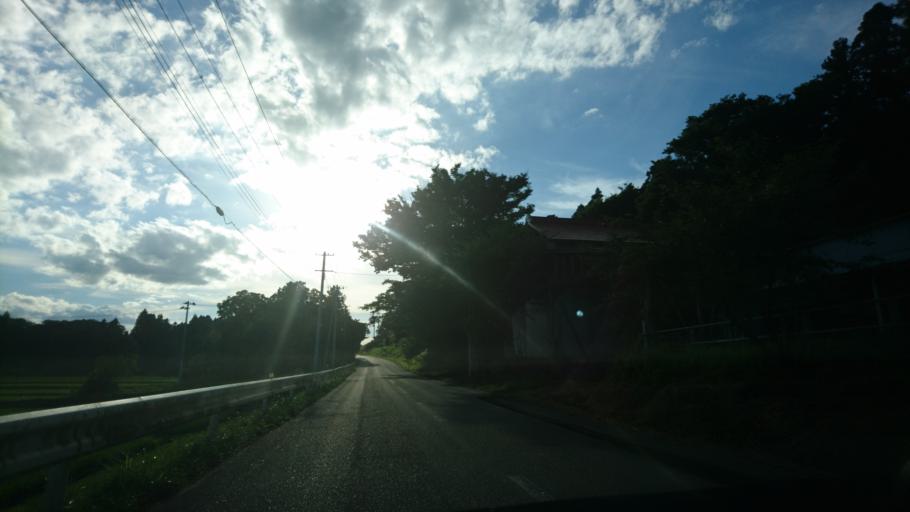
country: JP
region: Iwate
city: Ichinoseki
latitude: 38.8344
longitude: 141.1149
